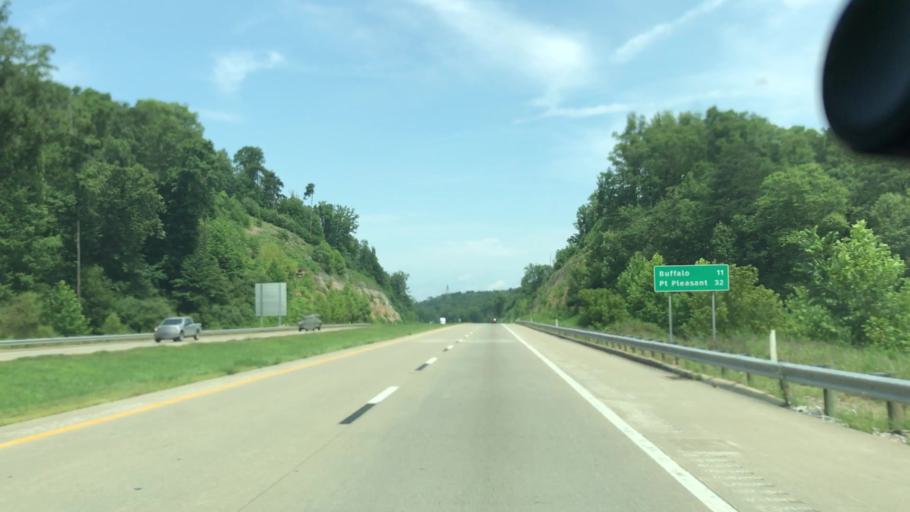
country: US
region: West Virginia
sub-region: Putnam County
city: Eleanor
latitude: 38.4949
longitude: -81.9326
